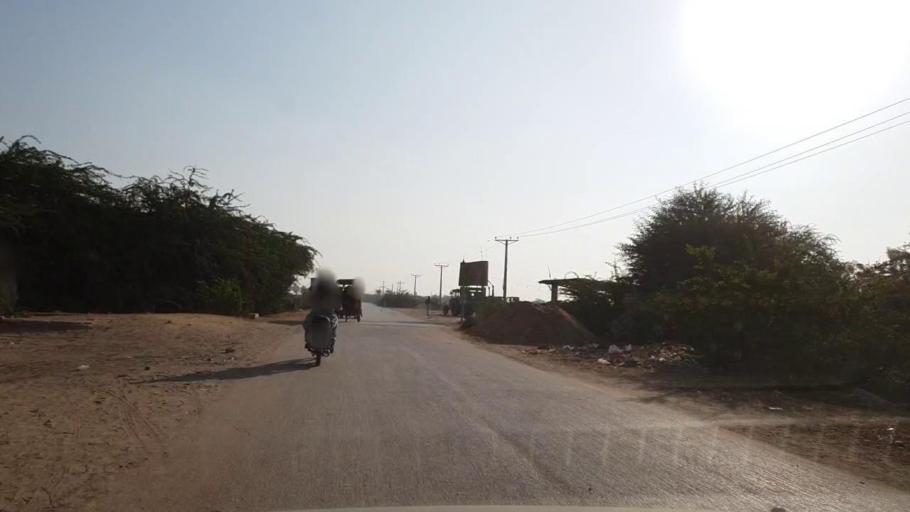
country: PK
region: Sindh
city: Bulri
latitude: 24.8608
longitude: 68.3297
